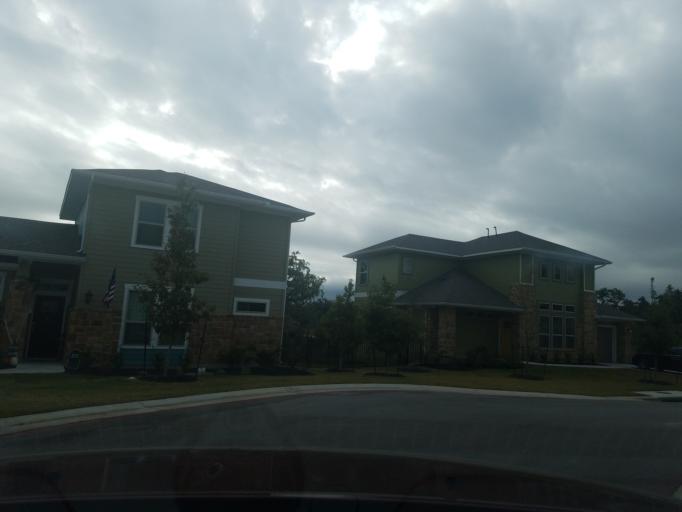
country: US
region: Texas
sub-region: Williamson County
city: Cedar Park
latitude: 30.4871
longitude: -97.7909
